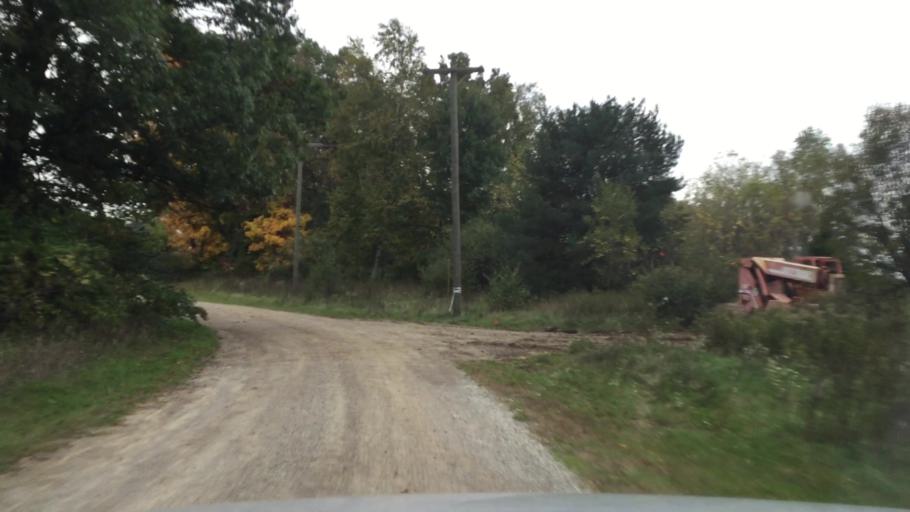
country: US
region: Michigan
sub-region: Genesee County
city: Fenton
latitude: 42.6797
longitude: -83.7393
